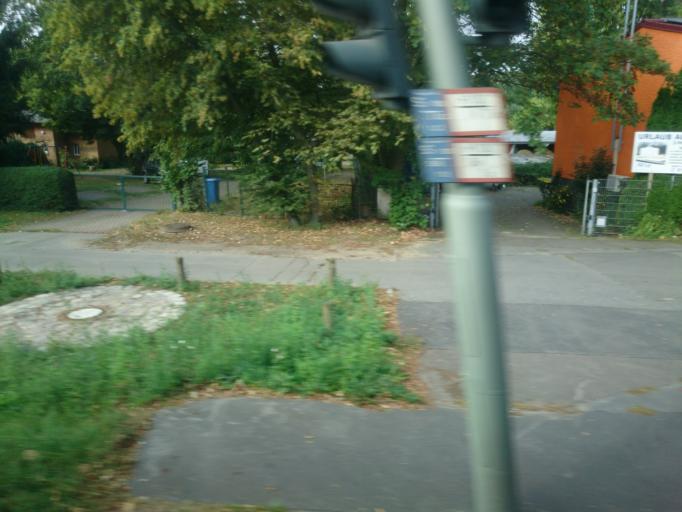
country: DE
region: Berlin
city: Stadtrandsiedlung Malchow
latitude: 52.5772
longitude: 13.4833
